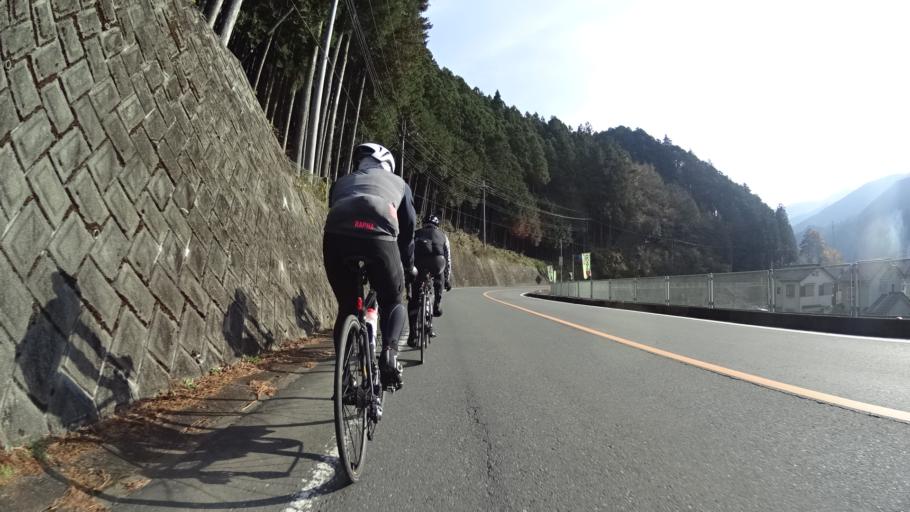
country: JP
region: Tokyo
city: Ome
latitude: 35.8740
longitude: 139.1874
